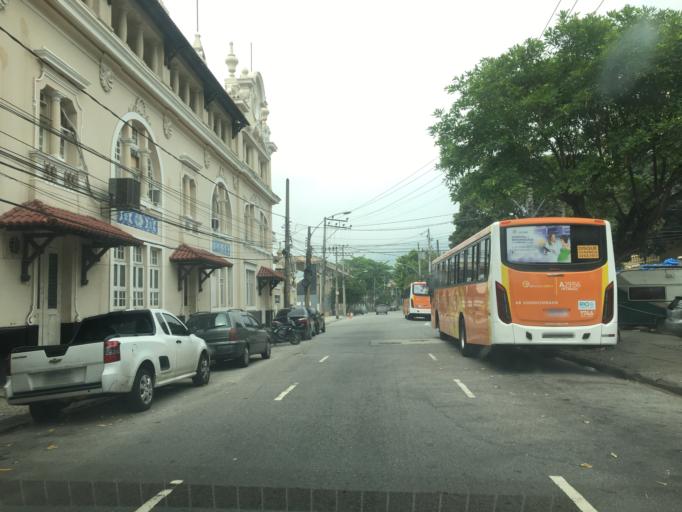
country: BR
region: Rio de Janeiro
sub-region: Rio De Janeiro
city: Rio de Janeiro
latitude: -22.8912
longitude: -43.2290
